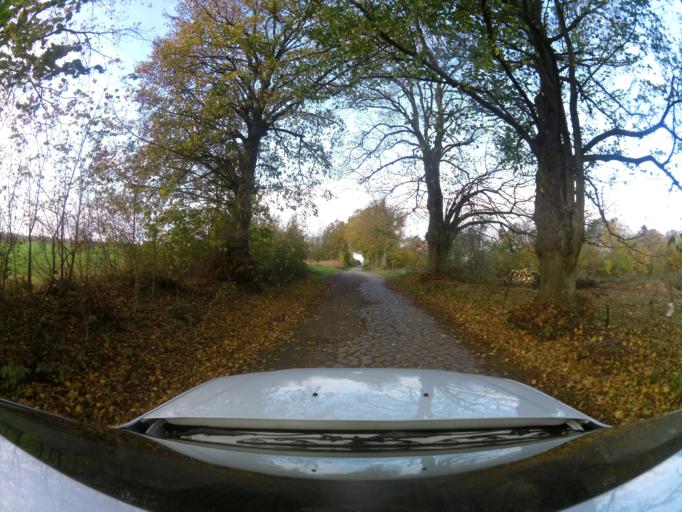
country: PL
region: West Pomeranian Voivodeship
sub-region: Powiat gryficki
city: Trzebiatow
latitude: 54.0472
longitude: 15.2130
